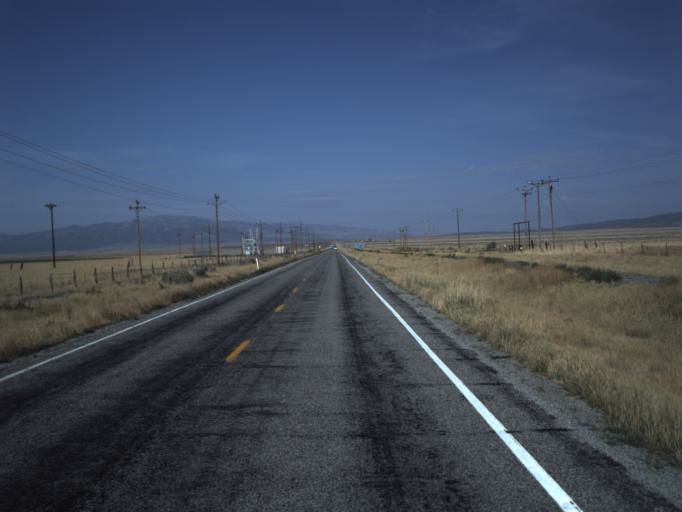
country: US
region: Idaho
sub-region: Oneida County
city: Malad City
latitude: 41.9663
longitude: -112.9393
